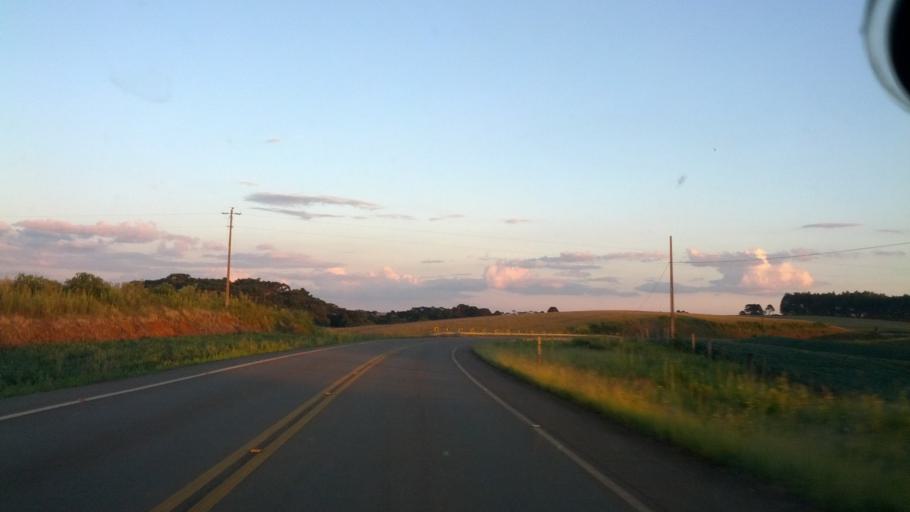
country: BR
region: Rio Grande do Sul
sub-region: Vacaria
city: Estrela
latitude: -27.8404
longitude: -50.8336
